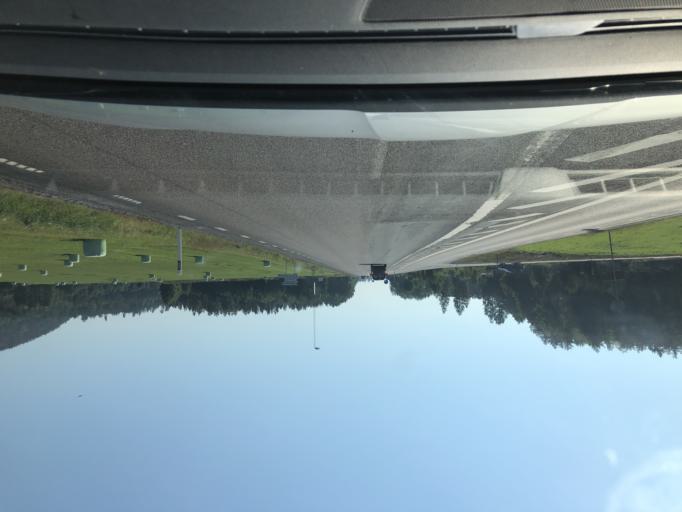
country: SE
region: Vaesternorrland
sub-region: Kramfors Kommun
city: Kramfors
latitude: 62.8755
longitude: 17.8562
